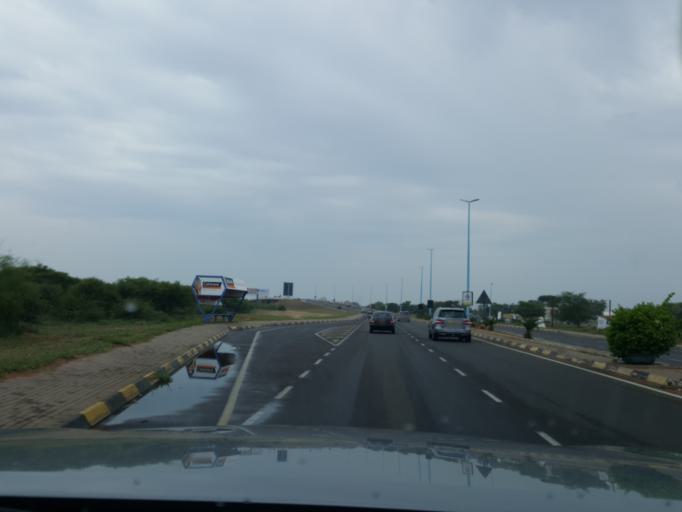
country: BW
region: South East
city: Gaborone
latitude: -24.6097
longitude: 25.9251
